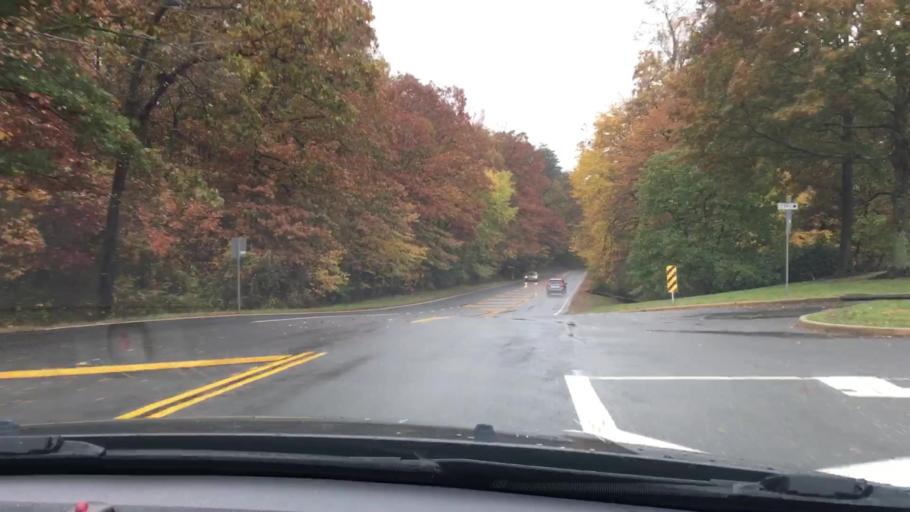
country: US
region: Virginia
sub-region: Fairfax County
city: Burke
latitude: 38.7537
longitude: -77.2780
